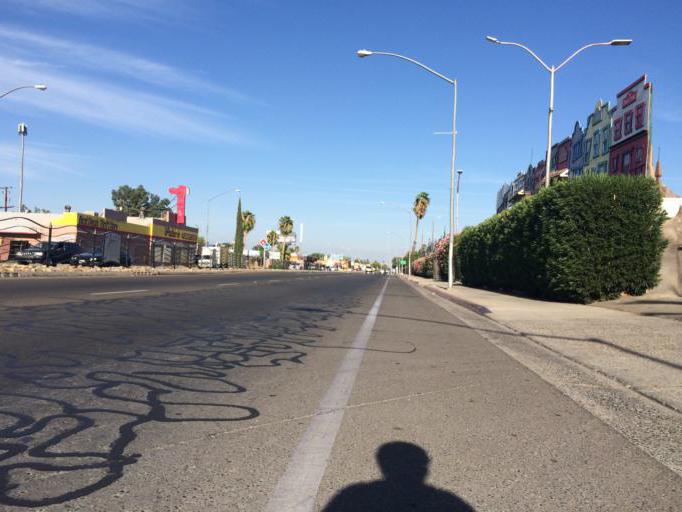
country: US
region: California
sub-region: Fresno County
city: Fresno
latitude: 36.7358
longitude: -119.7493
